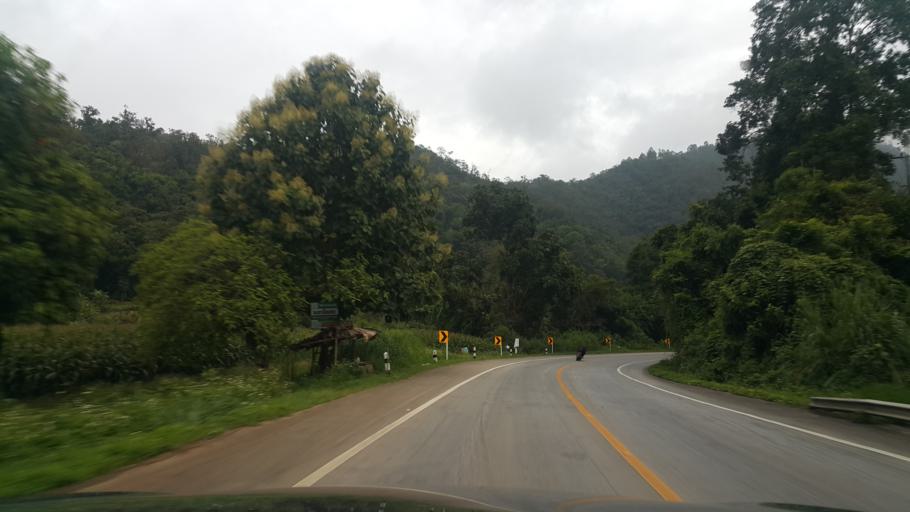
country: TH
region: Lampang
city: Wang Nuea
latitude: 19.1025
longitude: 99.4499
